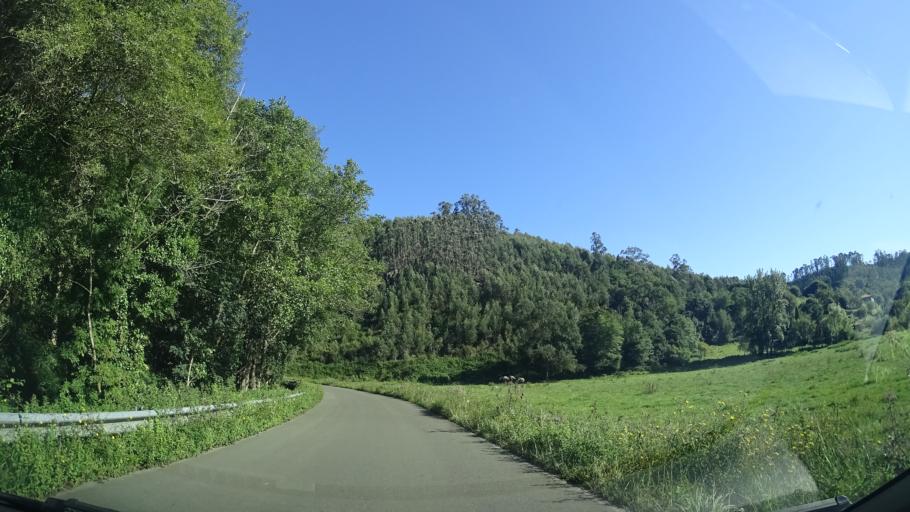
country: ES
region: Asturias
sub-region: Province of Asturias
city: Ribadesella
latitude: 43.4695
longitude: -5.1302
